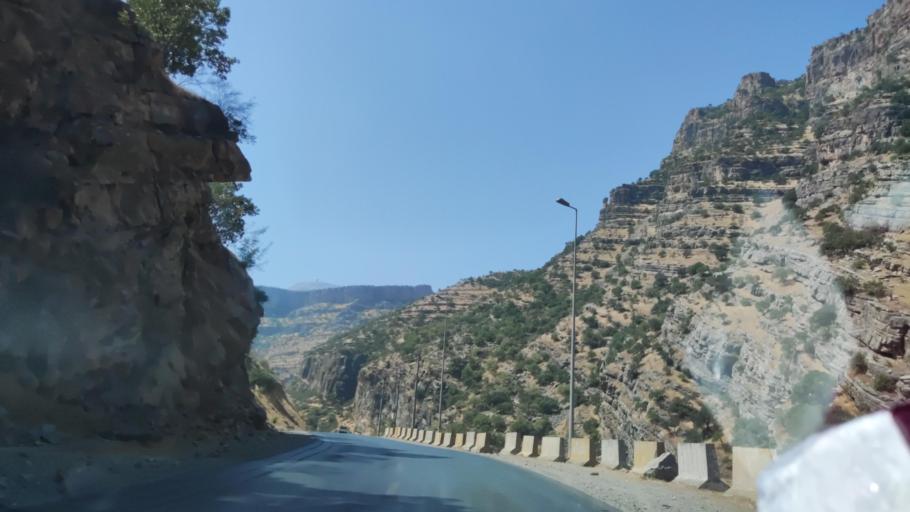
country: IQ
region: Arbil
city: Ruwandiz
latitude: 36.6428
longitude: 44.4936
